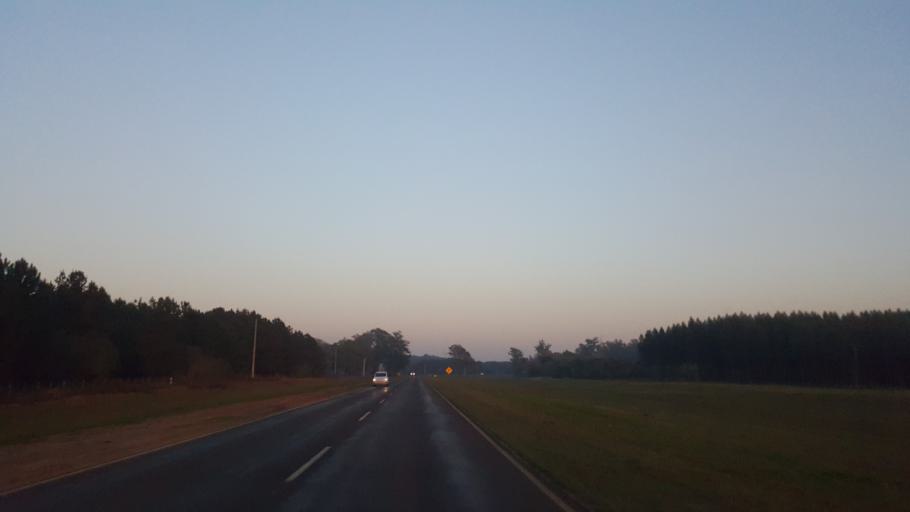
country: AR
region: Corrientes
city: Ituzaingo
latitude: -27.6164
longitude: -56.4181
